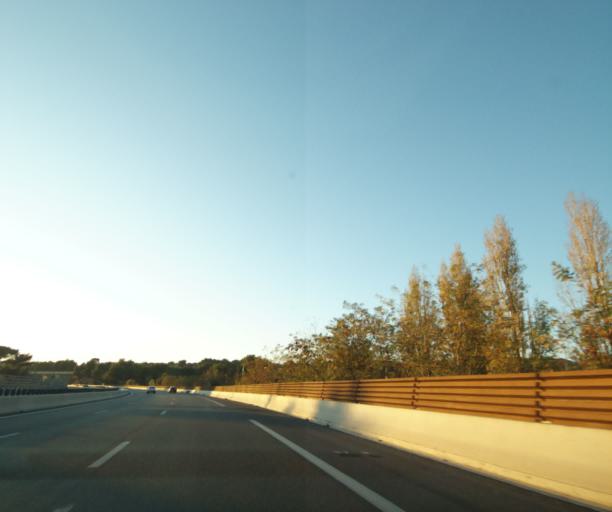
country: FR
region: Provence-Alpes-Cote d'Azur
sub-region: Departement des Bouches-du-Rhone
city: Ceyreste
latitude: 43.2098
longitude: 5.6263
